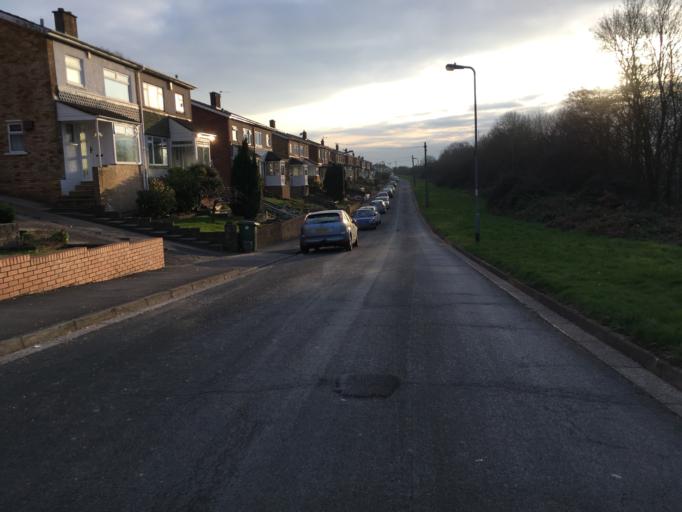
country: GB
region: Wales
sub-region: Cardiff
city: Cardiff
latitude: 51.5166
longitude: -3.1323
